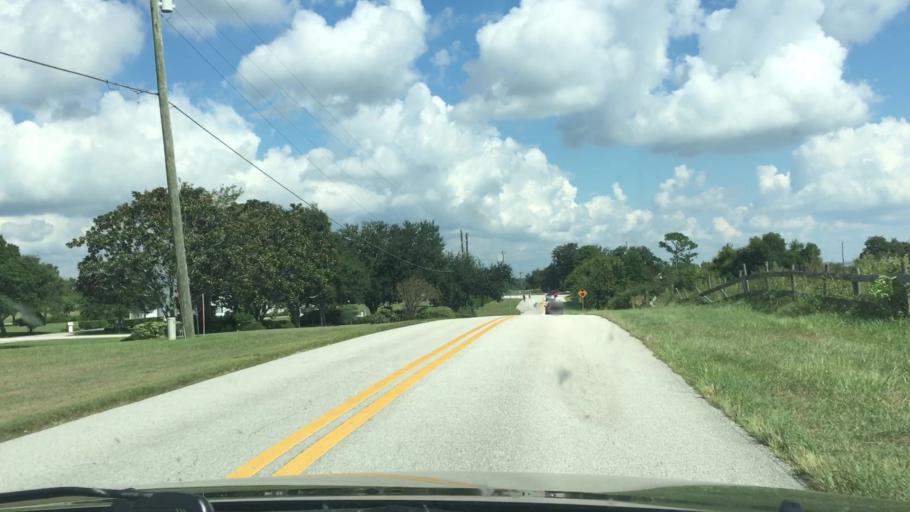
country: US
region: Florida
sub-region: Lake County
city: Montverde
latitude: 28.6030
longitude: -81.6901
